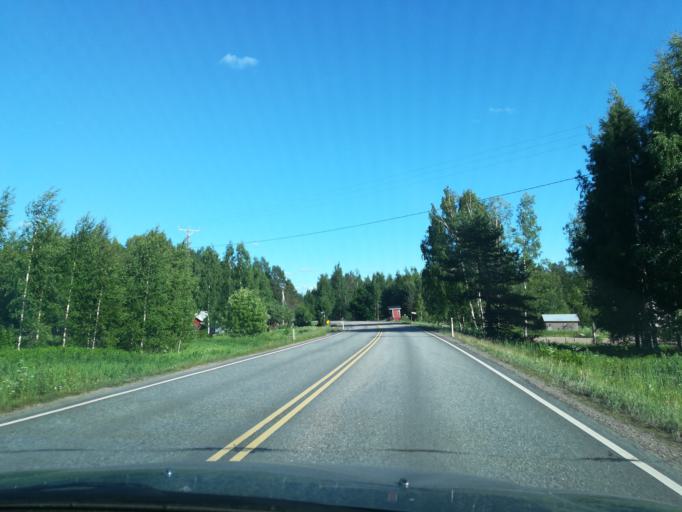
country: FI
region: South Karelia
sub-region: Imatra
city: Ruokolahti
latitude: 61.3542
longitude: 28.7219
